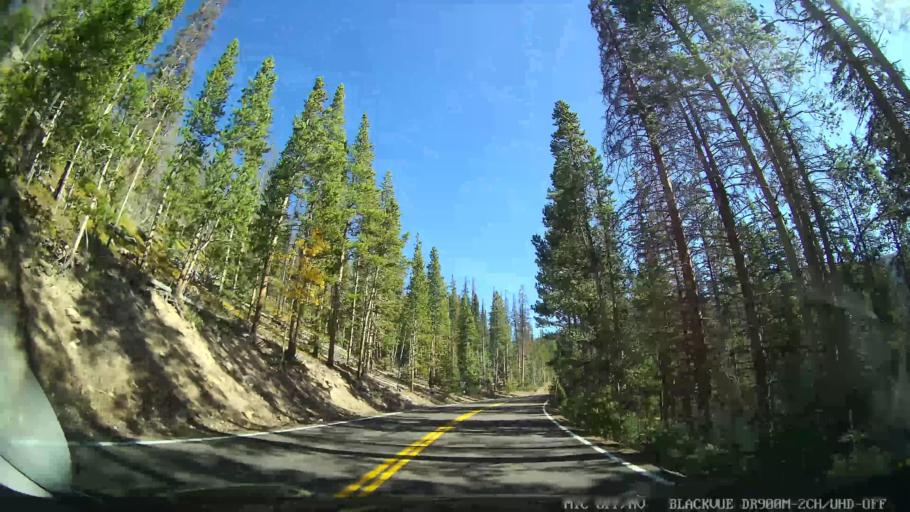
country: US
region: Colorado
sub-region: Larimer County
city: Estes Park
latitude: 40.4055
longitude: -105.8233
